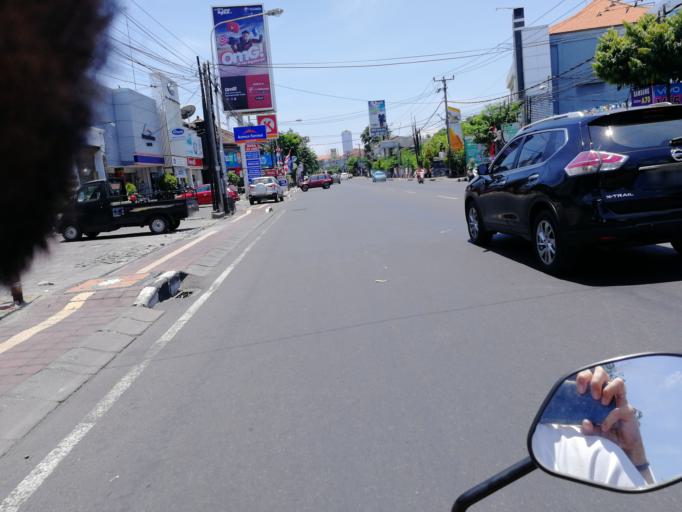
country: ID
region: Bali
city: Karyadharma
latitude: -8.6814
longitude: 115.1983
